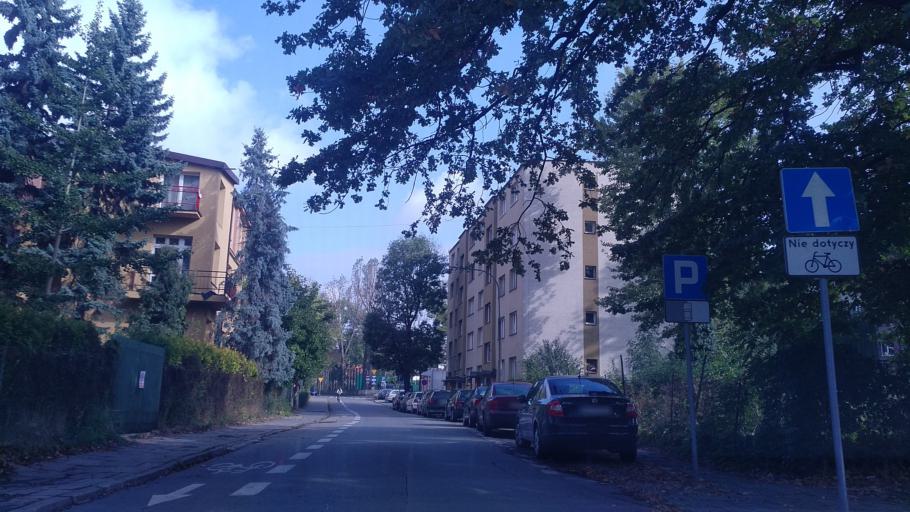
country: PL
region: Lesser Poland Voivodeship
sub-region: Krakow
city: Krakow
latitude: 50.0761
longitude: 19.9196
